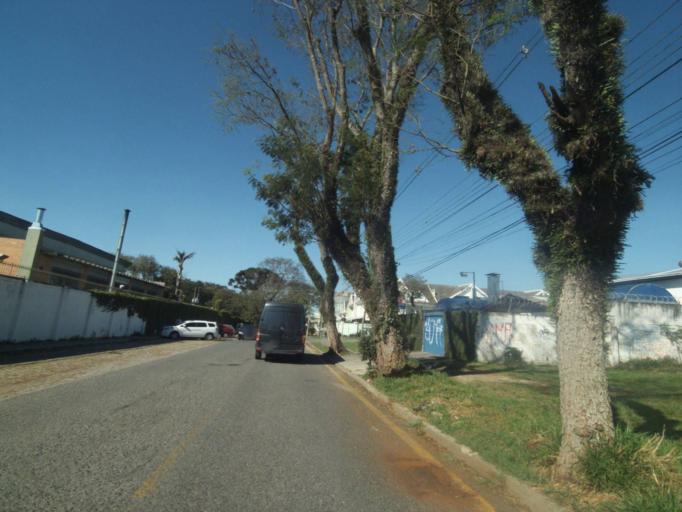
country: BR
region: Parana
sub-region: Curitiba
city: Curitiba
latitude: -25.3968
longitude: -49.2371
